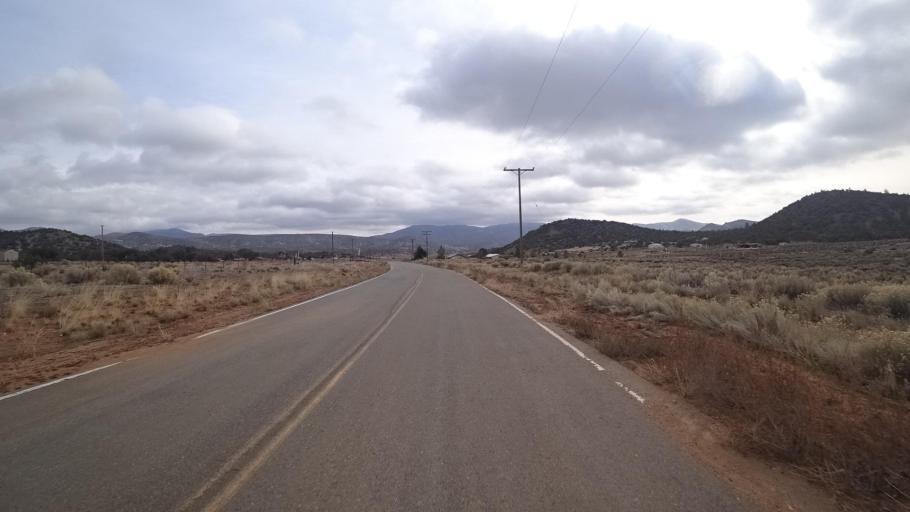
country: US
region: California
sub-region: Kern County
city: Tehachapi
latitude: 35.1748
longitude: -118.3530
